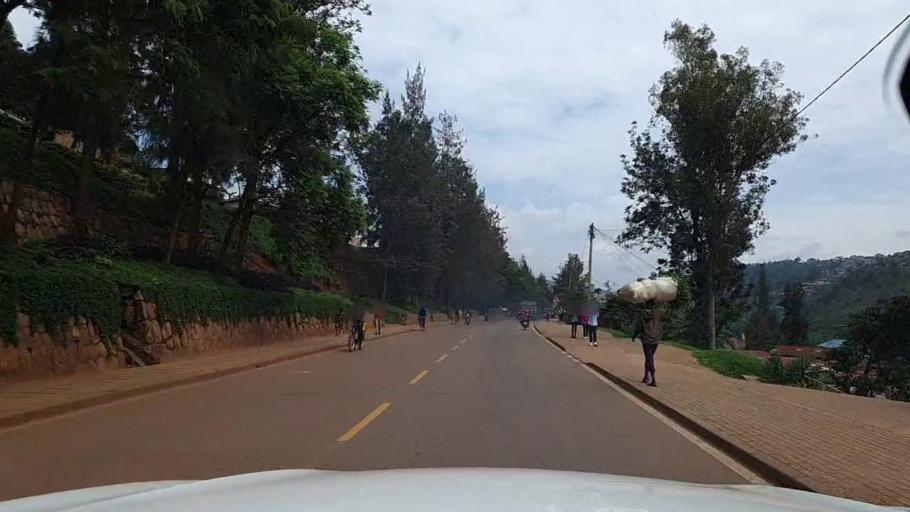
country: RW
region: Kigali
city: Kigali
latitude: -1.9307
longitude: 30.0458
